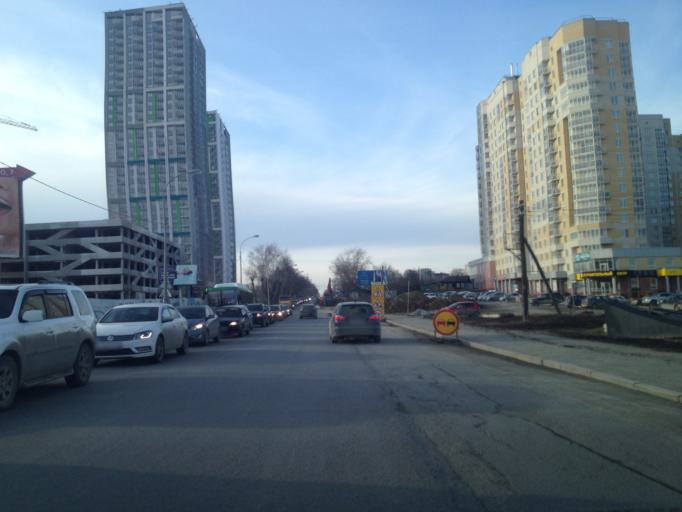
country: RU
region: Sverdlovsk
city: Yekaterinburg
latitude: 56.7987
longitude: 60.5951
